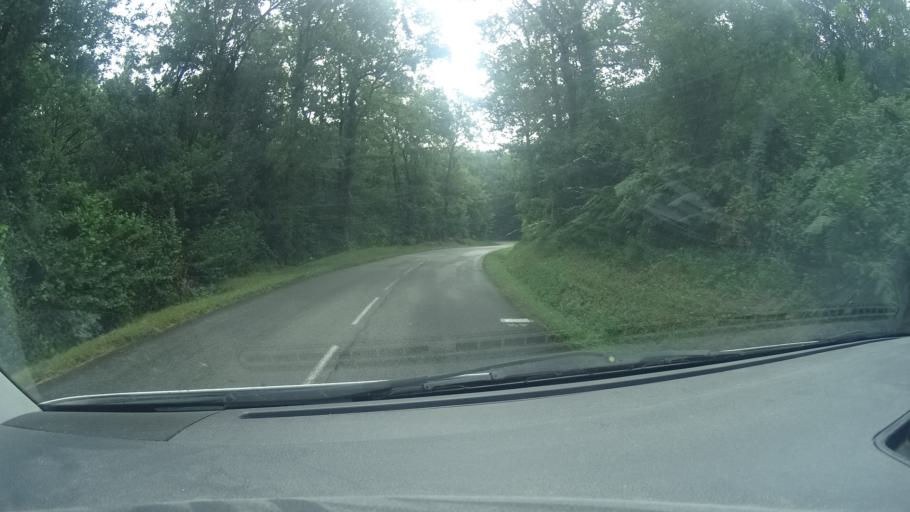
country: FR
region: Aquitaine
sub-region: Departement des Pyrenees-Atlantiques
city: Mont
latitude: 43.4872
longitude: -0.6929
